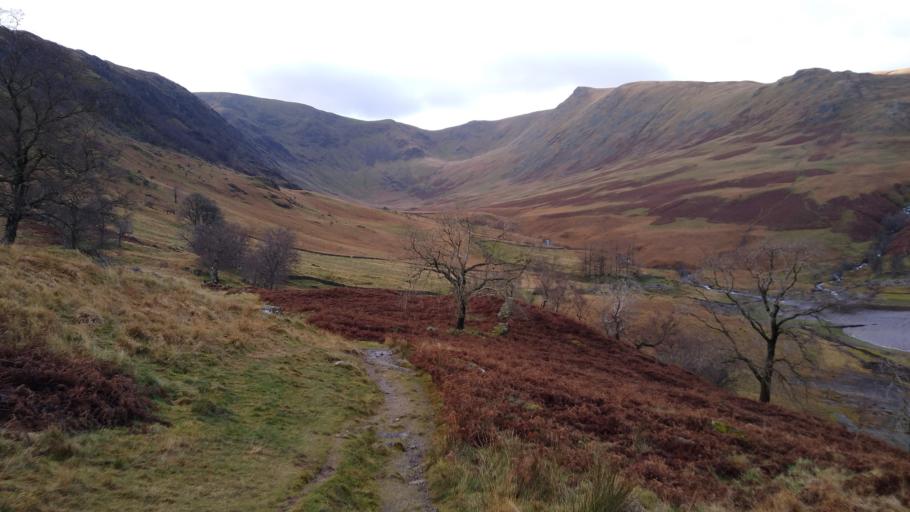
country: GB
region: England
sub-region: Cumbria
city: Windermere
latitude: 54.4961
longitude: -2.8157
